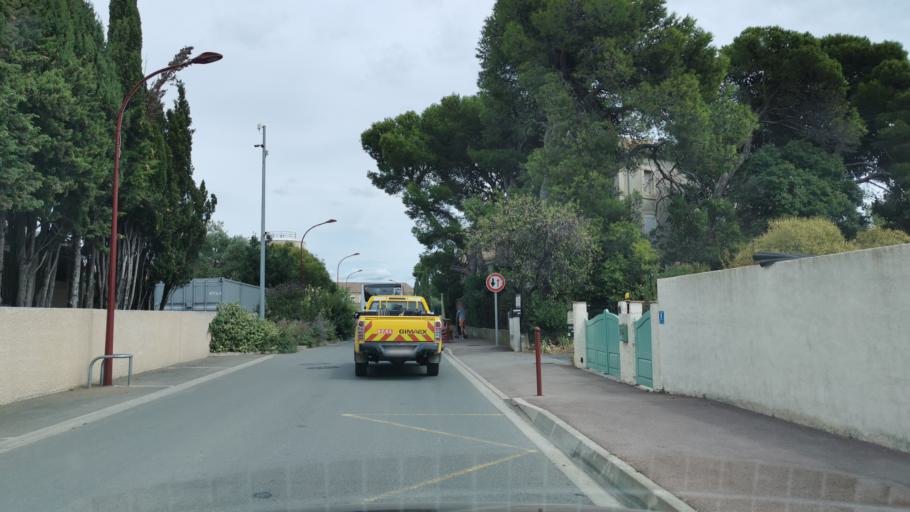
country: FR
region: Languedoc-Roussillon
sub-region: Departement de l'Aude
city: Argeliers
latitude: 43.3096
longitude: 2.9065
